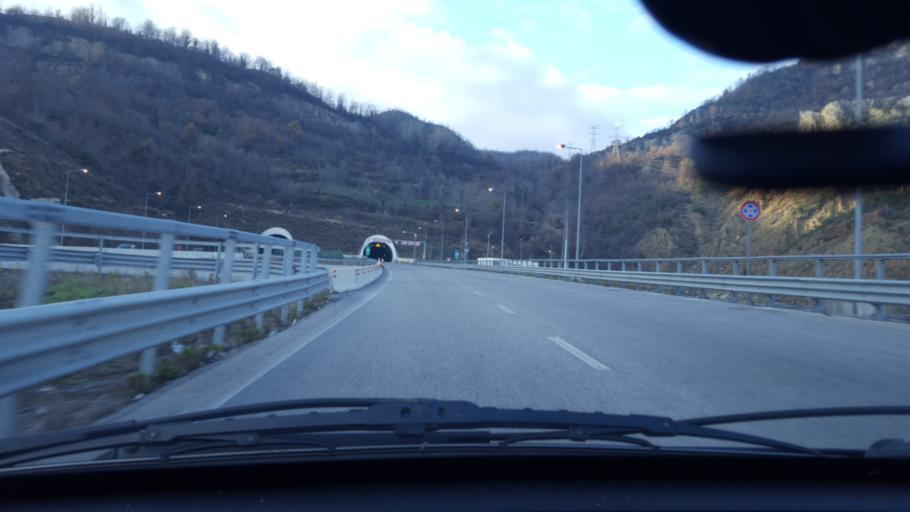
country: AL
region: Tirane
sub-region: Rrethi i Tiranes
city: Krrabe
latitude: 41.1947
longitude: 19.9883
